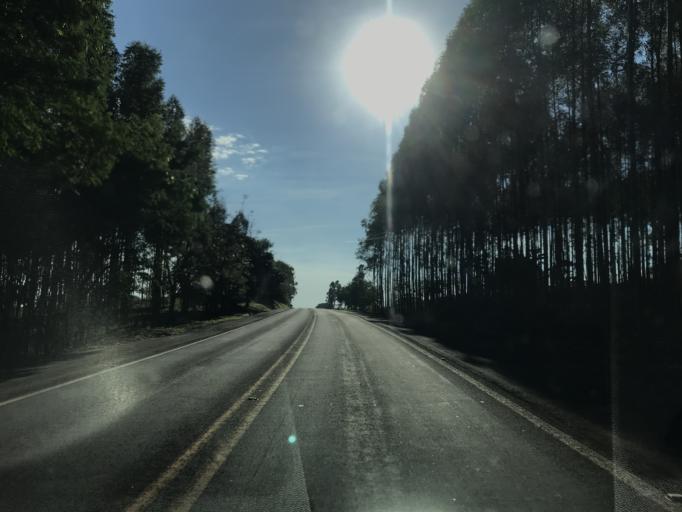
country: BR
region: Parana
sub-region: Ipora
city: Ipora
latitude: -24.0481
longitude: -53.7767
